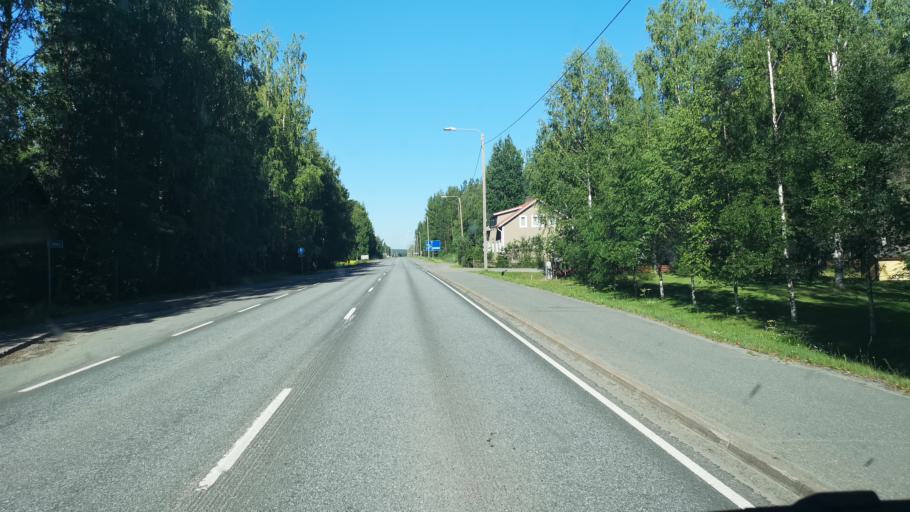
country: FI
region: Southern Ostrobothnia
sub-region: Seinaejoki
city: Lapua
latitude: 62.9695
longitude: 23.0617
